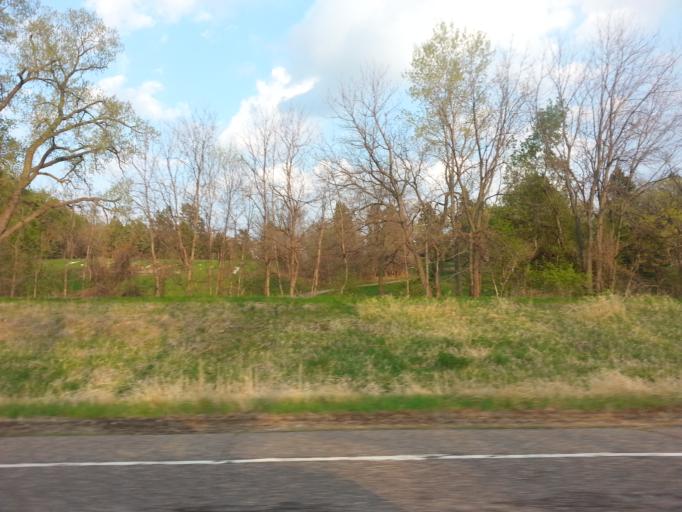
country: US
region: Minnesota
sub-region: Dakota County
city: Mendota Heights
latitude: 44.8806
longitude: -93.1726
